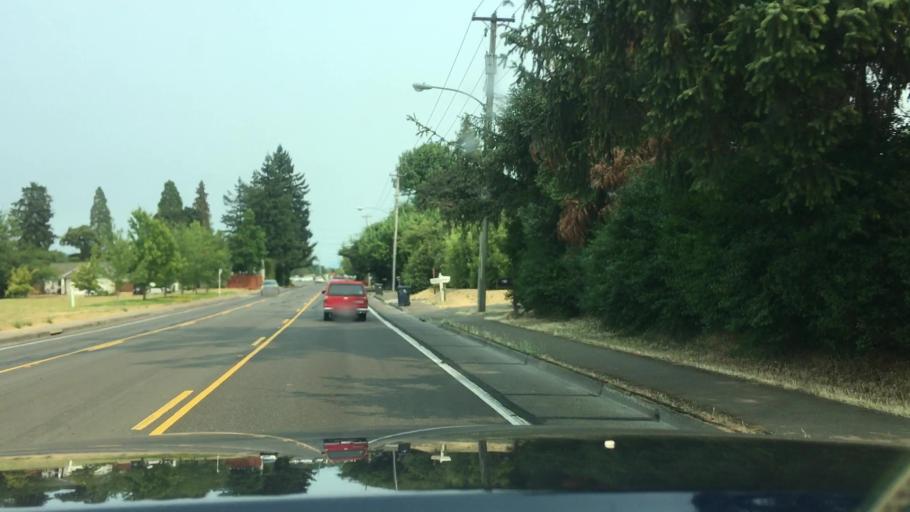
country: US
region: Oregon
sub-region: Lane County
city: Eugene
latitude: 44.0845
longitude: -123.1590
